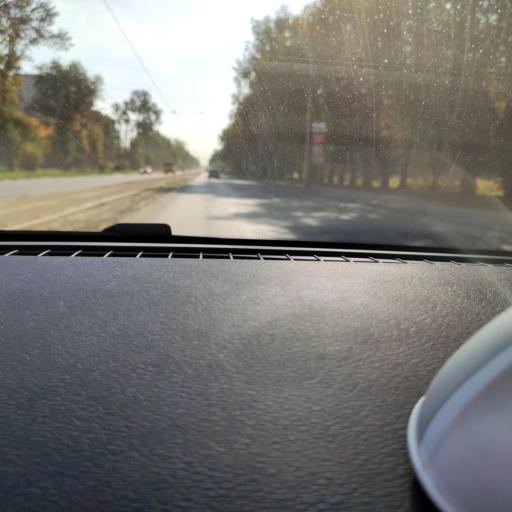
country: RU
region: Samara
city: Smyshlyayevka
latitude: 53.2017
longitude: 50.2853
